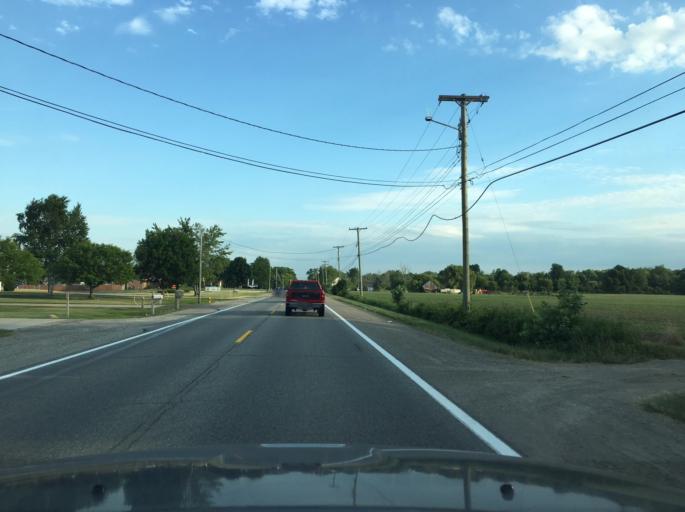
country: US
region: Michigan
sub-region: Macomb County
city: Mount Clemens
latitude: 42.6809
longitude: -82.8781
